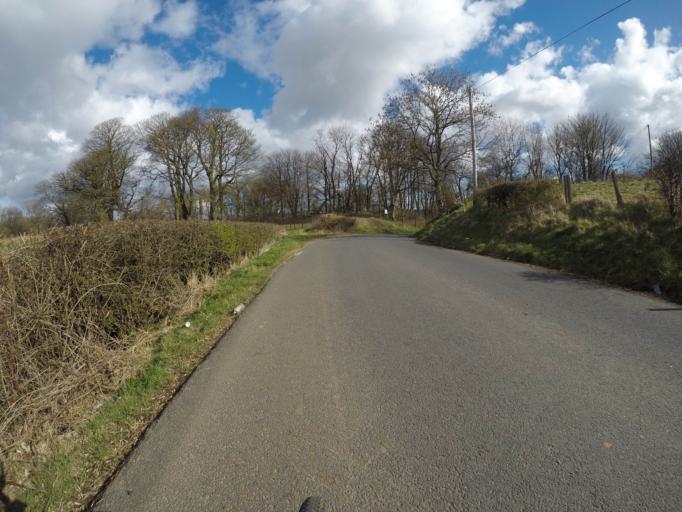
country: GB
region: Scotland
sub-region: North Ayrshire
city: Beith
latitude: 55.7287
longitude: -4.6068
